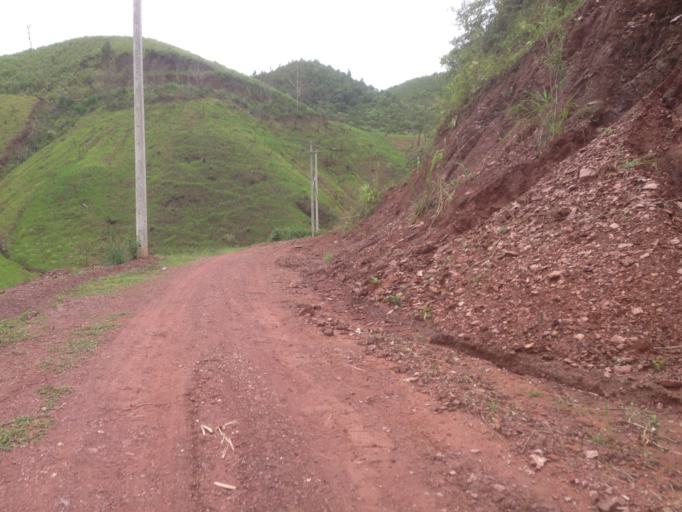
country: TH
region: Nan
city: Bo Kluea
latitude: 19.3919
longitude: 101.3286
